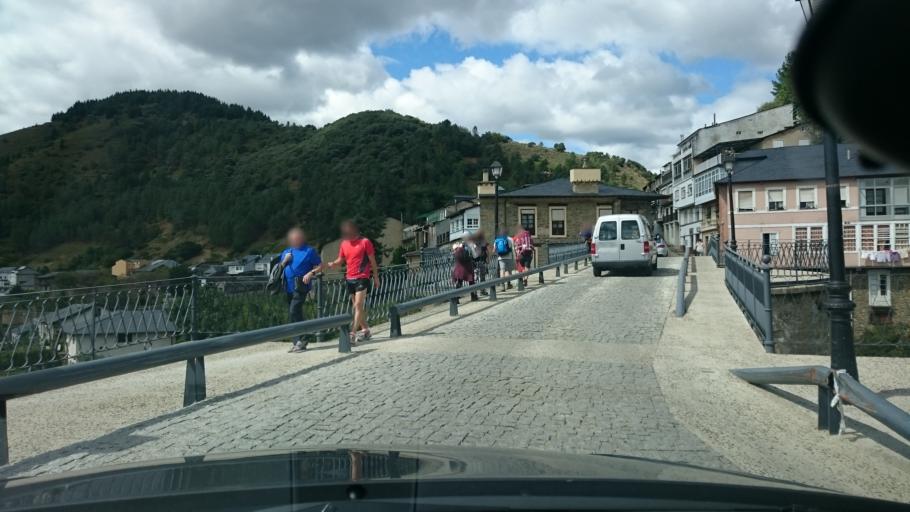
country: ES
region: Castille and Leon
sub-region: Provincia de Leon
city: Villafranca del Bierzo
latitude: 42.6090
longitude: -6.8113
